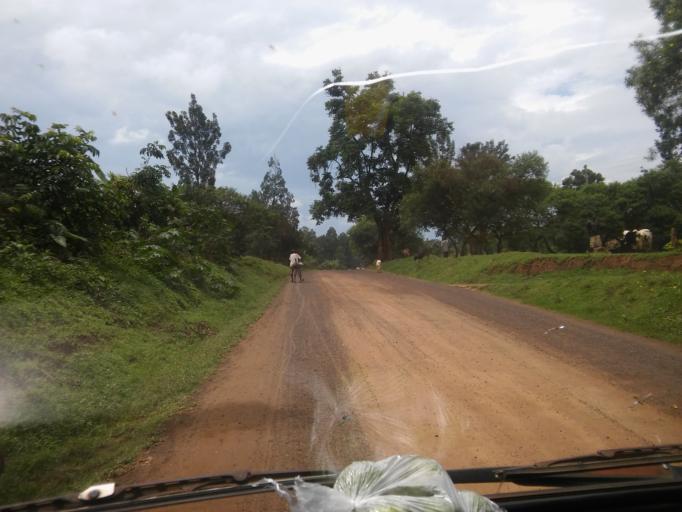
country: UG
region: Eastern Region
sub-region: Bududa District
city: Bududa
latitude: 0.9508
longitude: 34.2656
